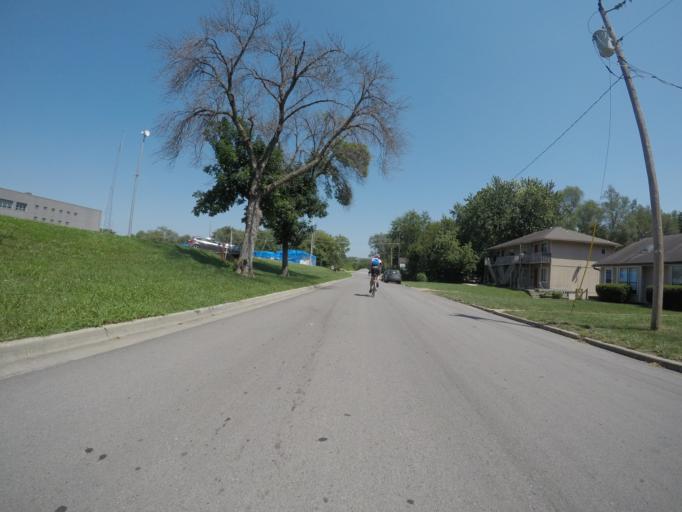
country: US
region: Kansas
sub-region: Leavenworth County
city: Leavenworth
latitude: 39.3133
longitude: -94.9107
